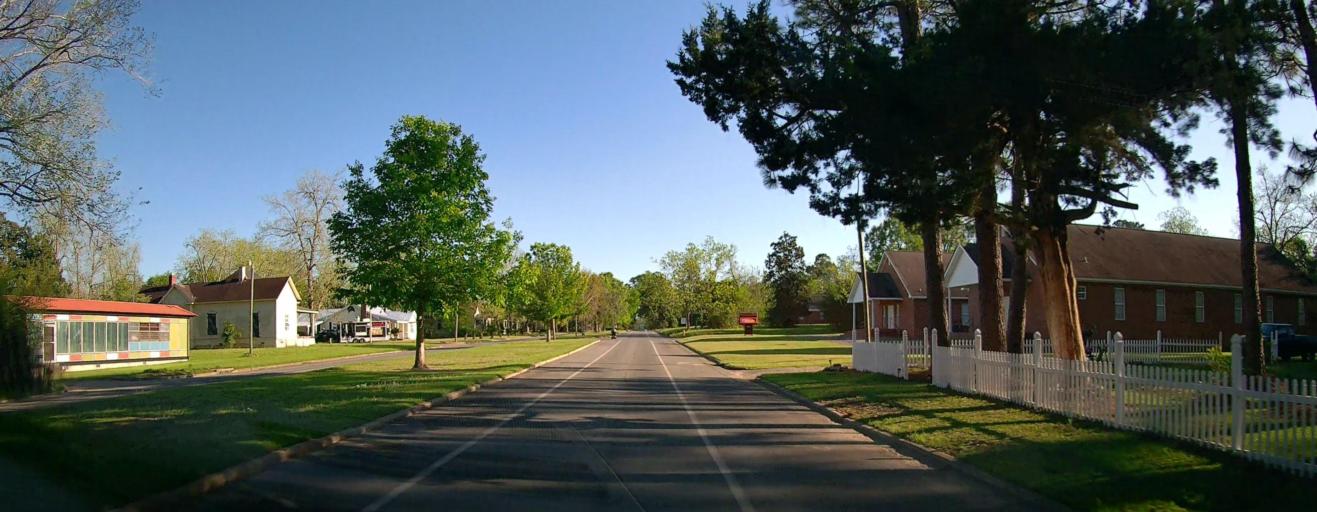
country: US
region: Georgia
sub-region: Ben Hill County
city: Fitzgerald
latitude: 31.7215
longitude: -83.2546
